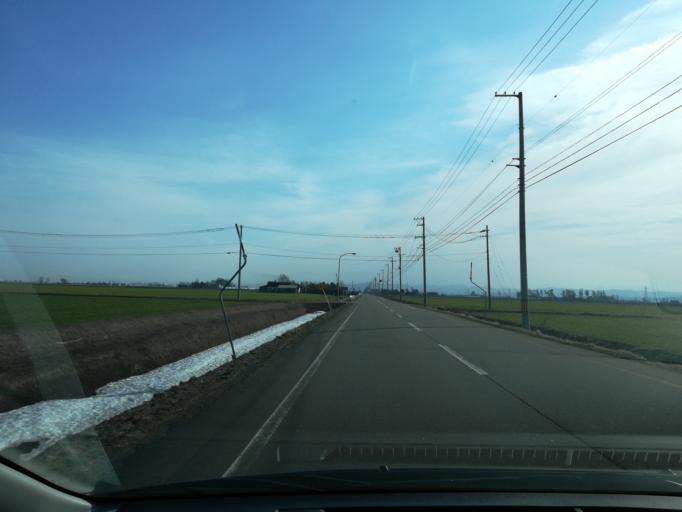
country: JP
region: Hokkaido
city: Iwamizawa
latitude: 43.1684
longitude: 141.6642
